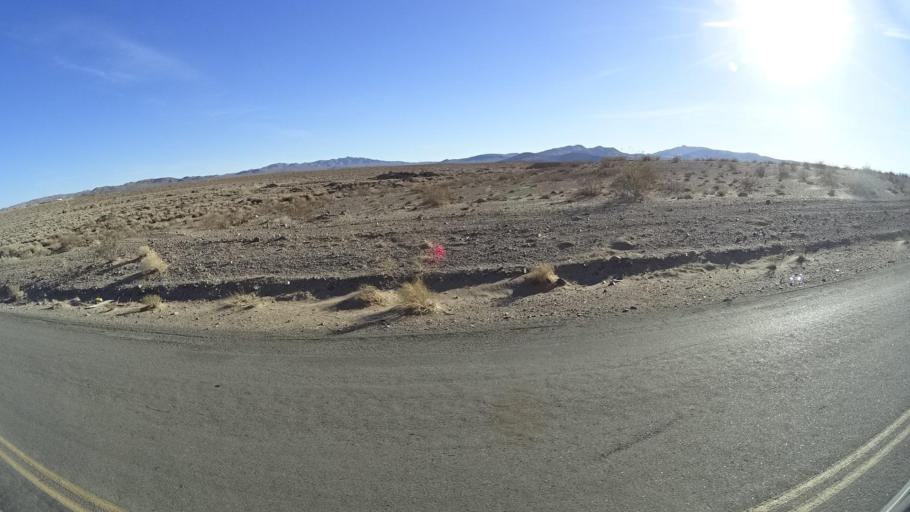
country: US
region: California
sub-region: Kern County
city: China Lake Acres
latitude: 35.6077
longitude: -117.7533
